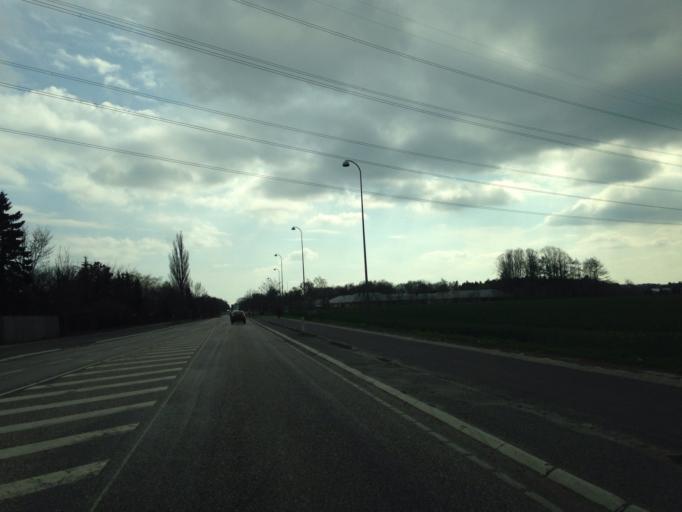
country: DK
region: Capital Region
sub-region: Hoje-Taastrup Kommune
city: Taastrup
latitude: 55.6328
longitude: 12.2859
